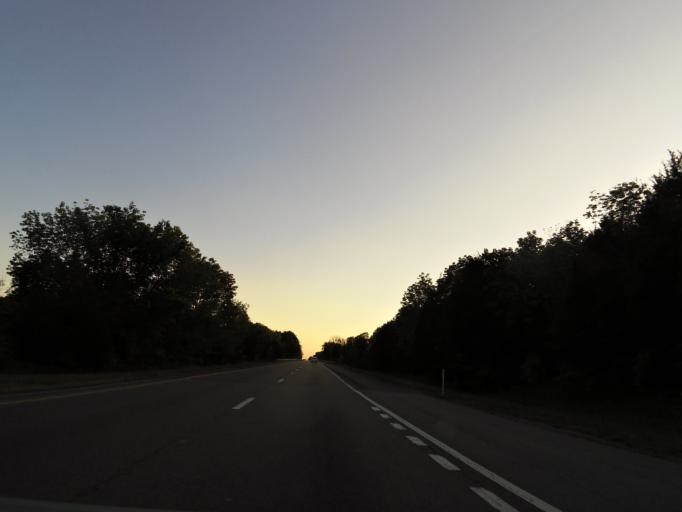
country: US
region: Tennessee
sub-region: Greene County
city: Mosheim
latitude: 36.2707
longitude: -82.9308
